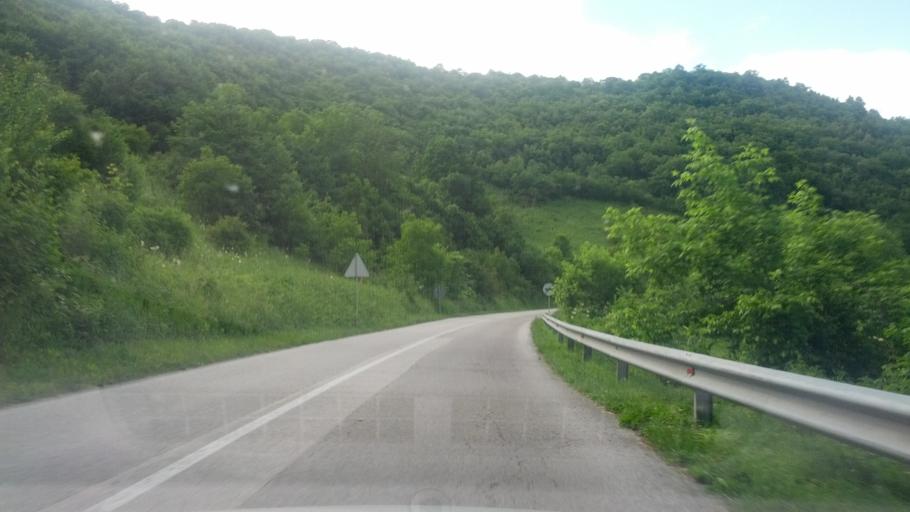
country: BA
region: Federation of Bosnia and Herzegovina
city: Stijena
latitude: 44.9036
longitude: 15.9915
